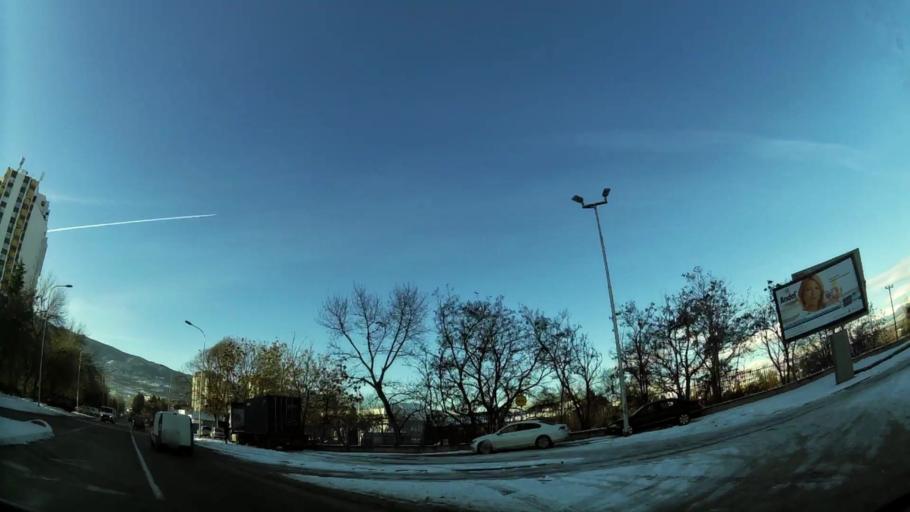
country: MK
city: Krushopek
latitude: 42.0097
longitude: 21.3848
